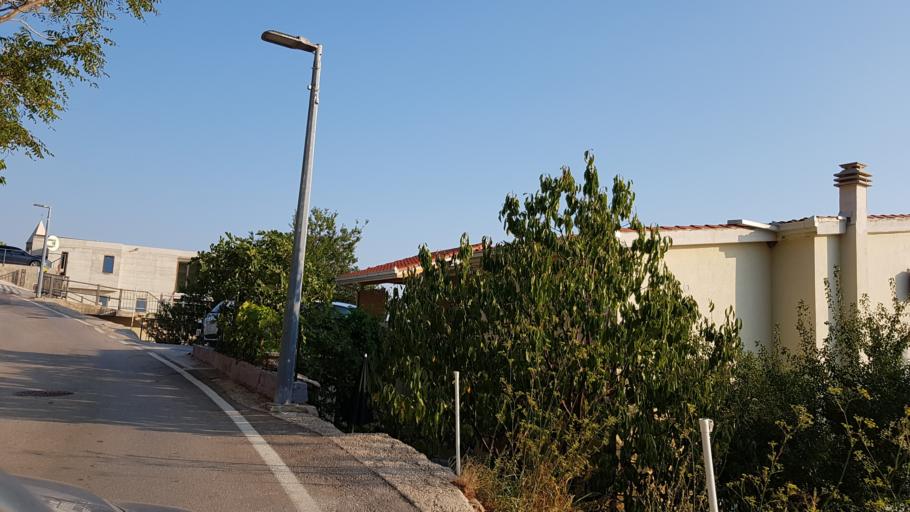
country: HR
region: Splitsko-Dalmatinska
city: Donja Brela
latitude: 43.3853
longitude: 16.9058
